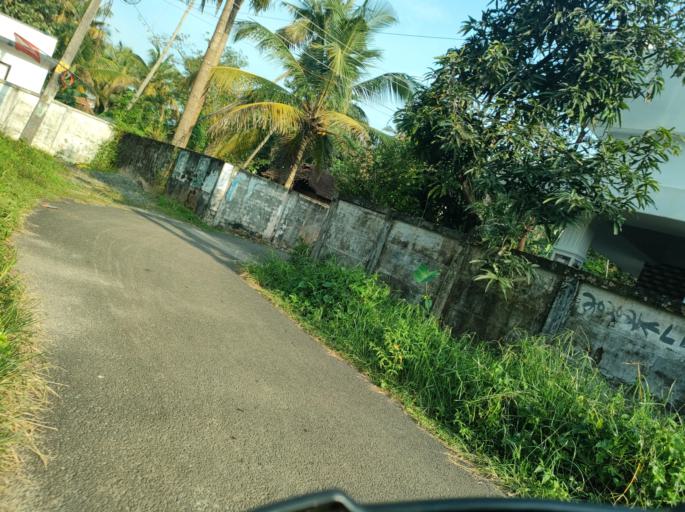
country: IN
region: Kerala
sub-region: Ernakulam
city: Elur
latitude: 10.0634
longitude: 76.2116
